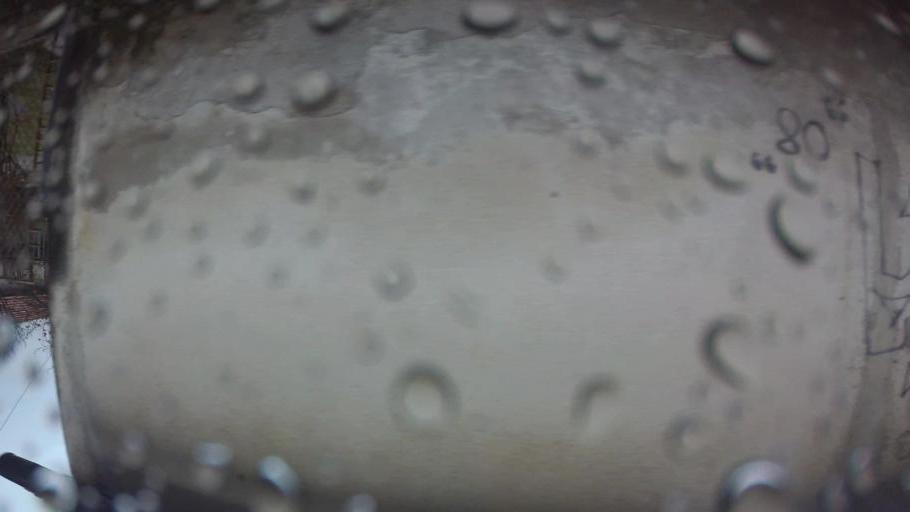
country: BA
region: Federation of Bosnia and Herzegovina
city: Cim
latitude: 43.3475
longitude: 17.7845
